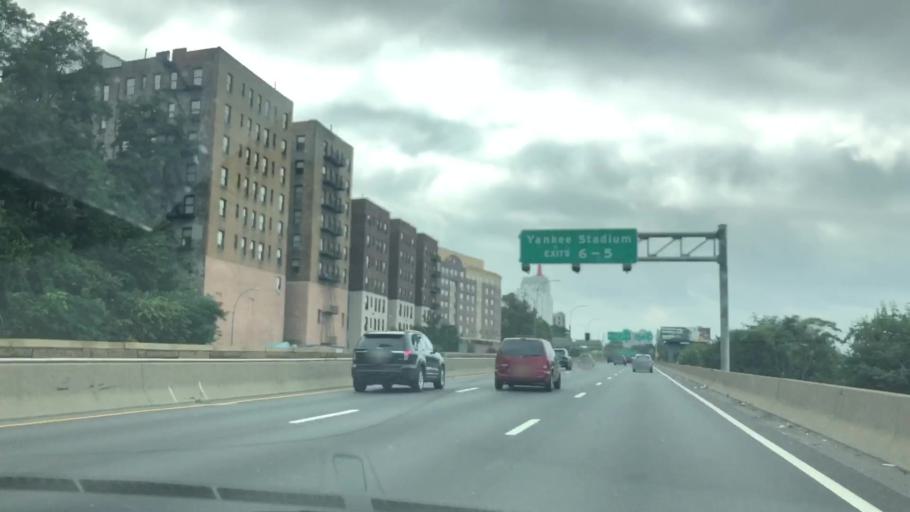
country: US
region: New York
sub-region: New York County
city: Inwood
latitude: 40.8357
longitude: -73.9311
